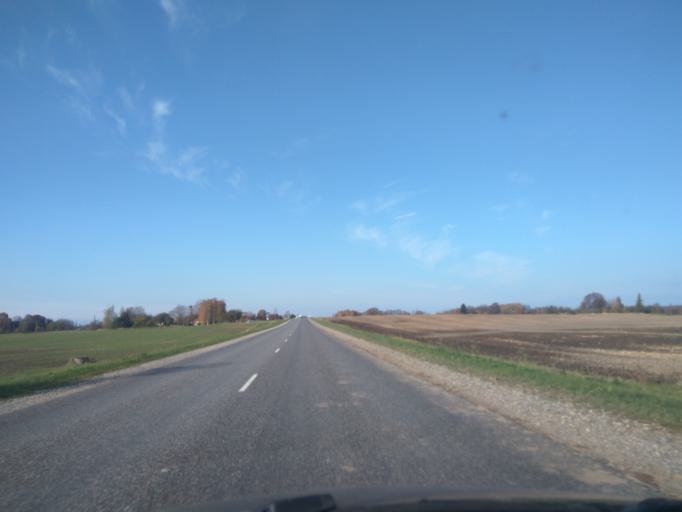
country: LV
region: Kuldigas Rajons
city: Kuldiga
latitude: 56.9922
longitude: 21.9114
